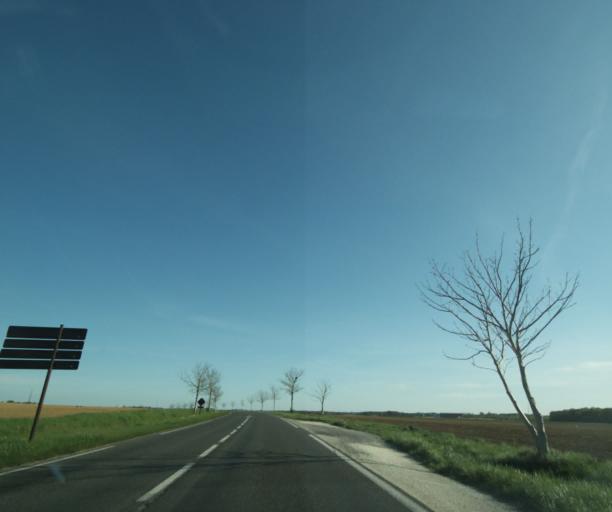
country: FR
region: Ile-de-France
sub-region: Departement de Seine-et-Marne
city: Nangis
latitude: 48.5549
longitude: 2.9968
